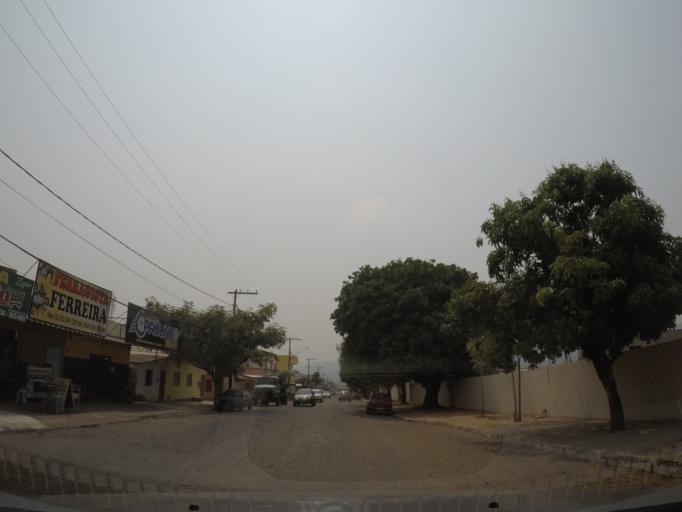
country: BR
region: Goias
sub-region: Pirenopolis
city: Pirenopolis
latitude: -15.8586
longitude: -48.9572
